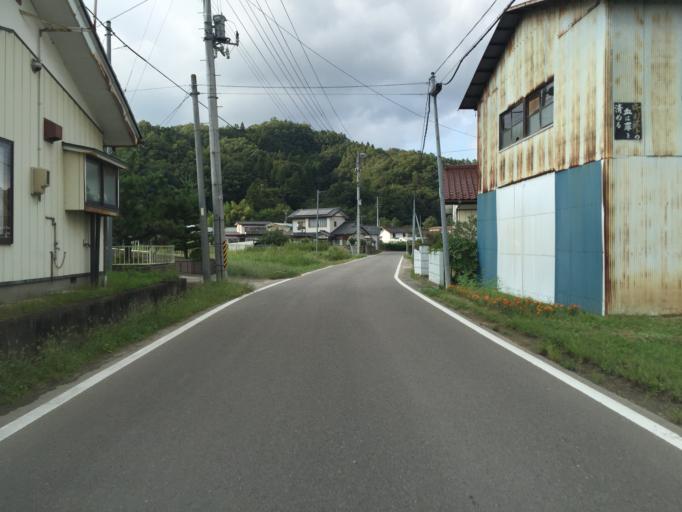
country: JP
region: Fukushima
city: Hobaramachi
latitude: 37.7150
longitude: 140.6028
